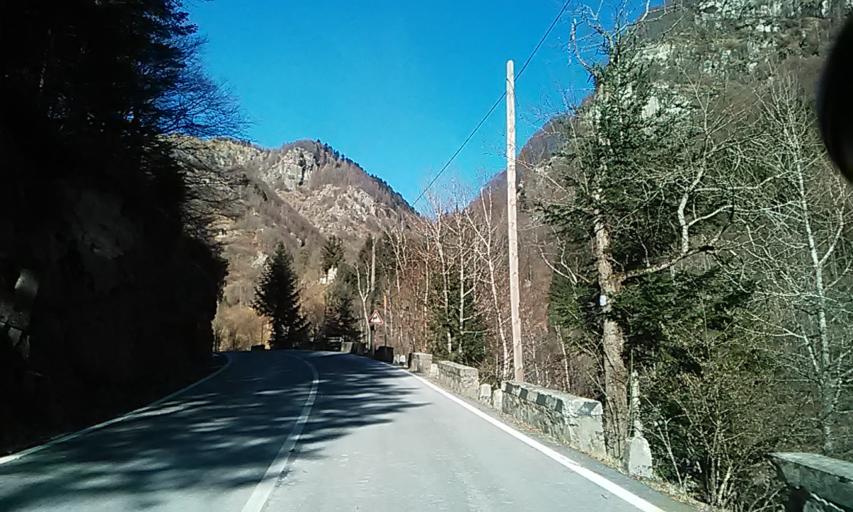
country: IT
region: Piedmont
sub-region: Provincia di Vercelli
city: Rimasco
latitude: 45.8758
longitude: 8.0699
